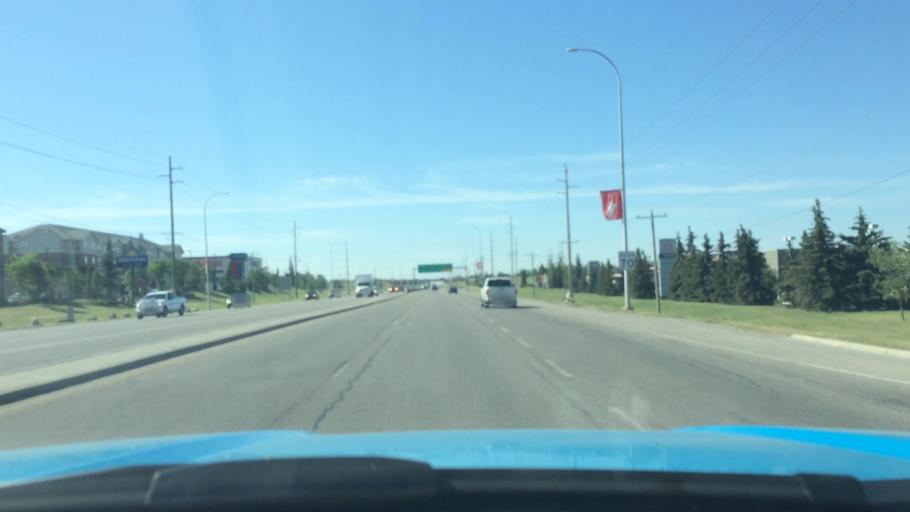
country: CA
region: Alberta
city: Calgary
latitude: 51.0732
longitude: -114.0018
